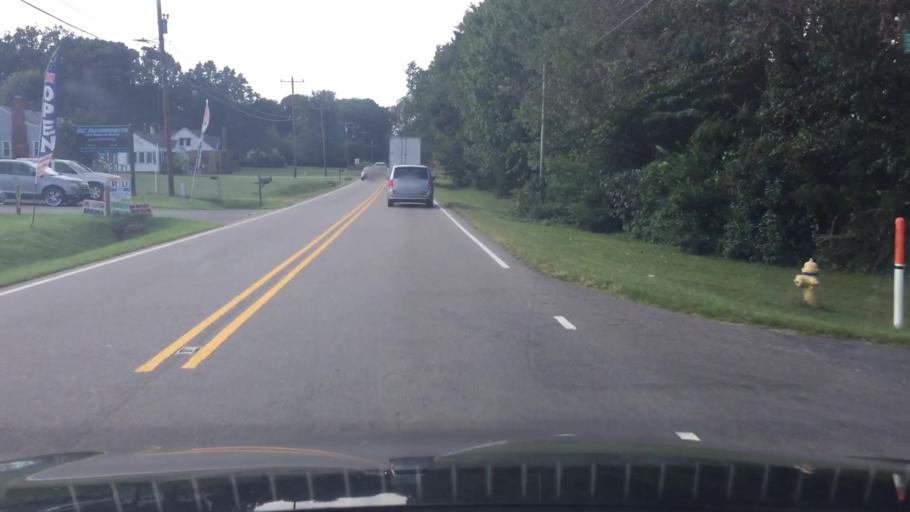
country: US
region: North Carolina
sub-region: Iredell County
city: Mooresville
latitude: 35.6175
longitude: -80.8234
